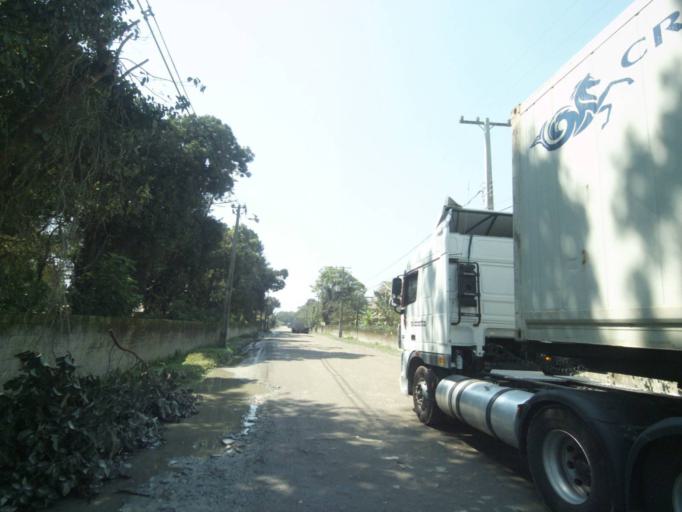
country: BR
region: Parana
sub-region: Paranagua
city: Paranagua
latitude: -25.5492
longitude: -48.5778
